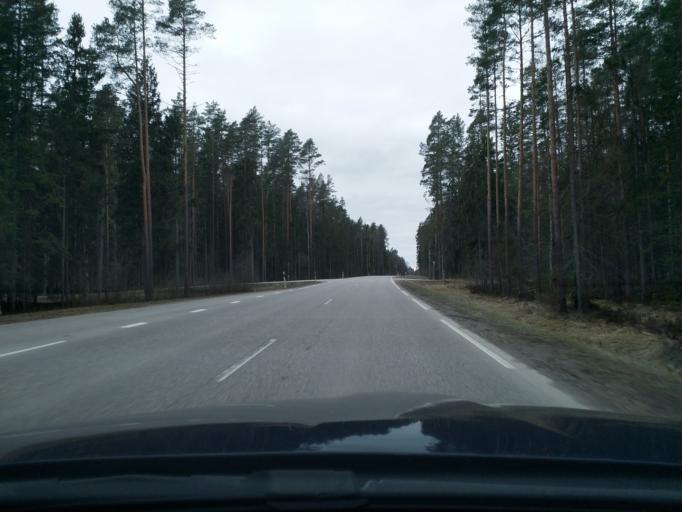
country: LV
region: Kuldigas Rajons
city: Kuldiga
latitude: 56.9509
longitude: 22.1609
